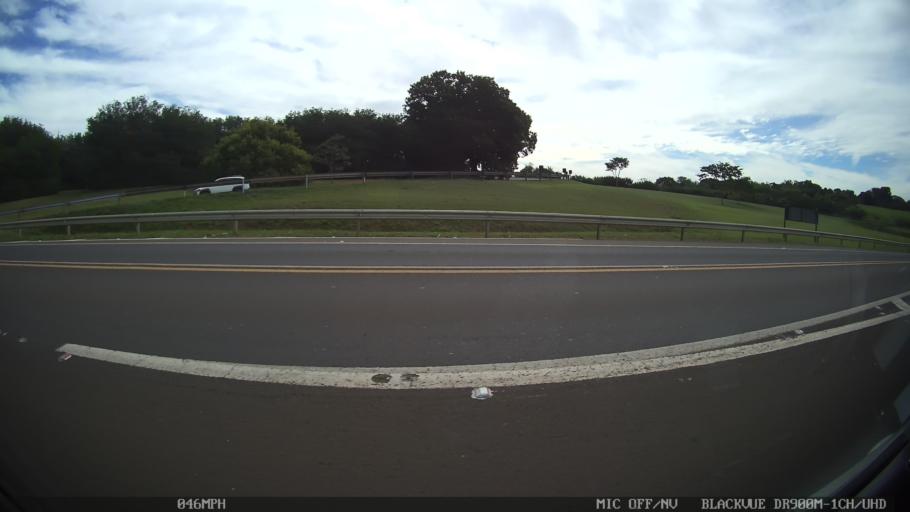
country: BR
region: Sao Paulo
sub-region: Taquaritinga
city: Taquaritinga
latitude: -21.4751
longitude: -48.5973
